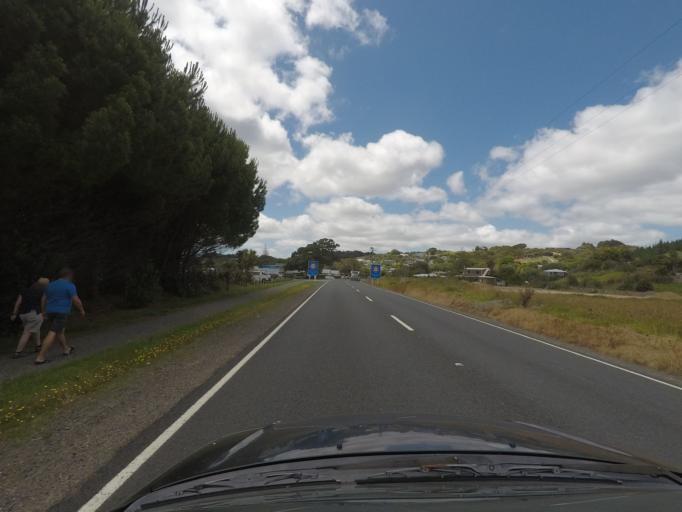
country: NZ
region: Northland
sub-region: Whangarei
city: Ruakaka
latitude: -36.0260
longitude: 174.5013
